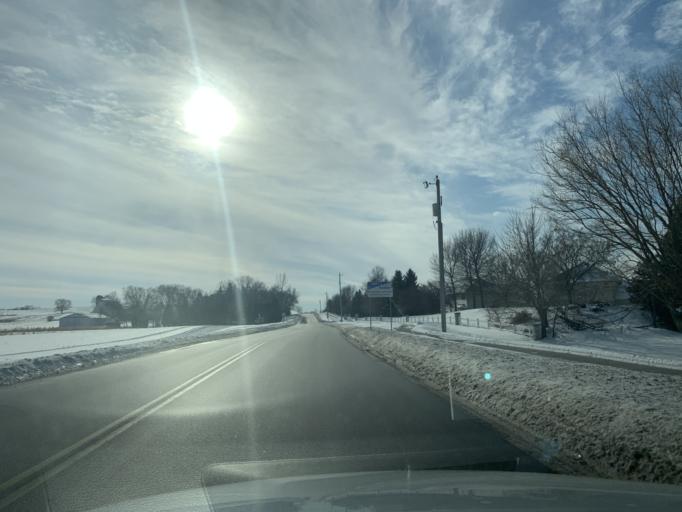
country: US
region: Minnesota
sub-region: Wright County
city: Albertville
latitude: 45.2226
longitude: -93.6441
